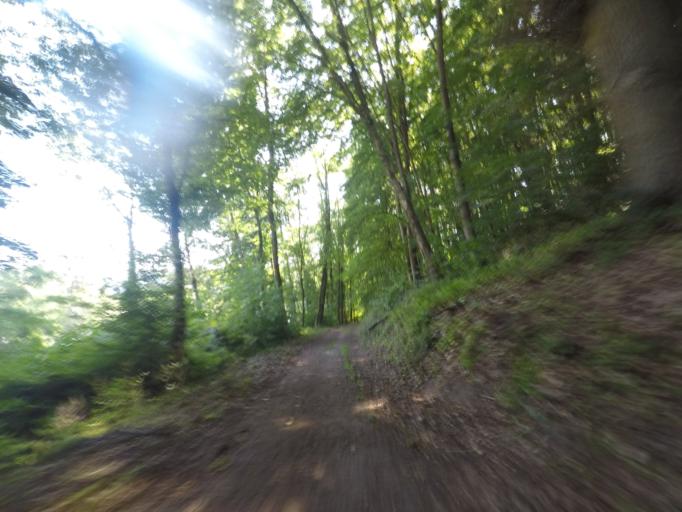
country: LU
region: Luxembourg
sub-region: Canton de Luxembourg
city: Luxembourg
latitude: 49.6314
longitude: 6.1168
